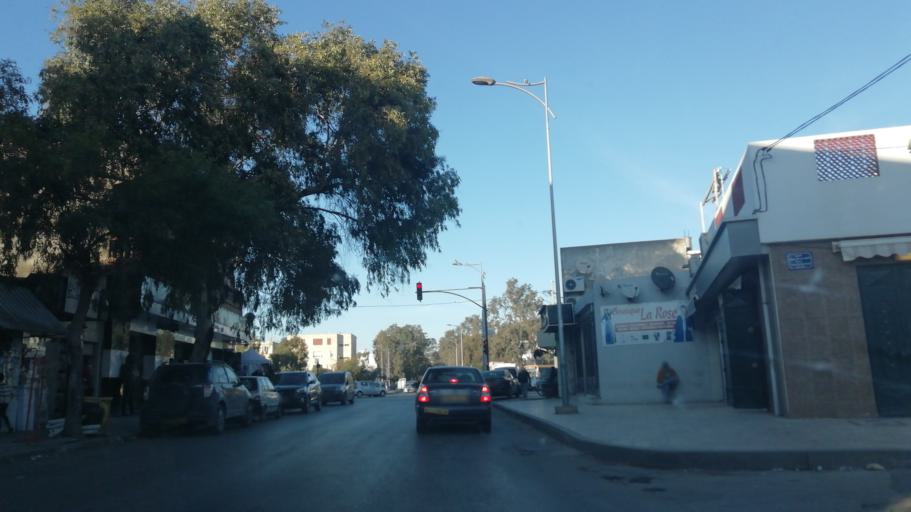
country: DZ
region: Oran
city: Oran
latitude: 35.7108
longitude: -0.6039
